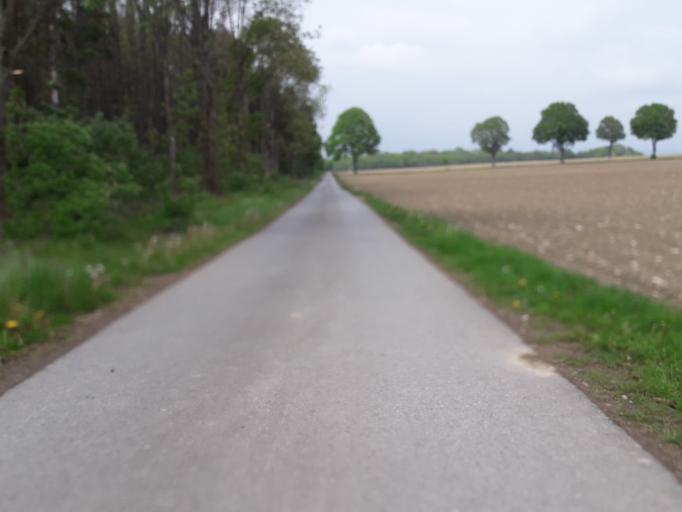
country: DE
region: North Rhine-Westphalia
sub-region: Regierungsbezirk Detmold
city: Paderborn
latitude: 51.6846
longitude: 8.7574
